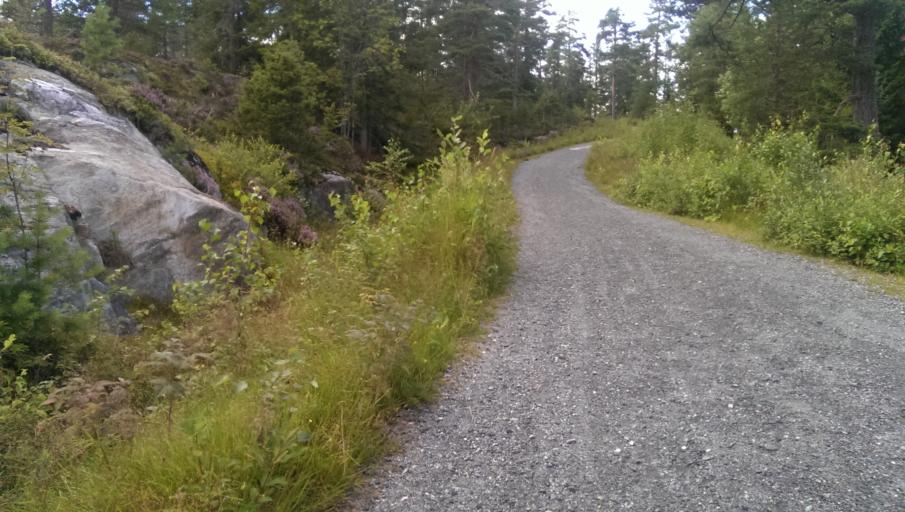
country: NO
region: Buskerud
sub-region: Kongsberg
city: Kongsberg
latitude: 59.6525
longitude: 9.6097
